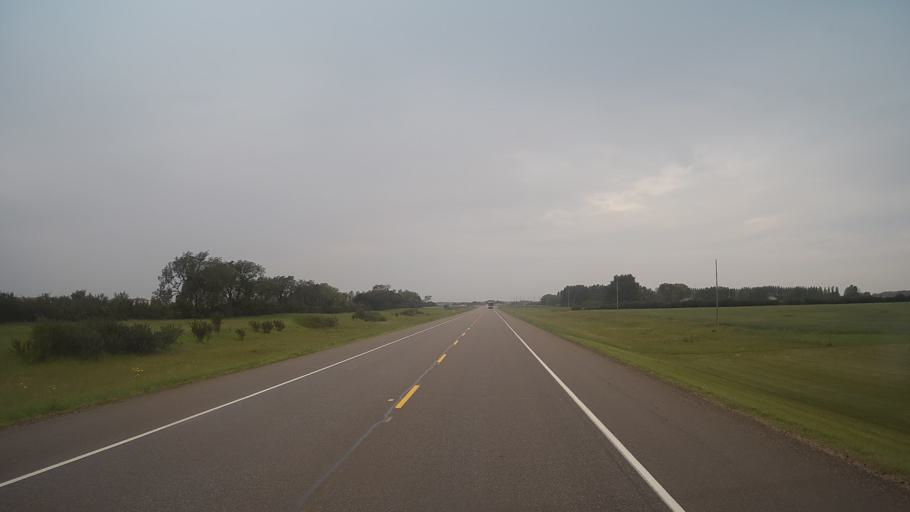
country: CA
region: Saskatchewan
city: Dalmeny
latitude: 52.1292
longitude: -106.8738
